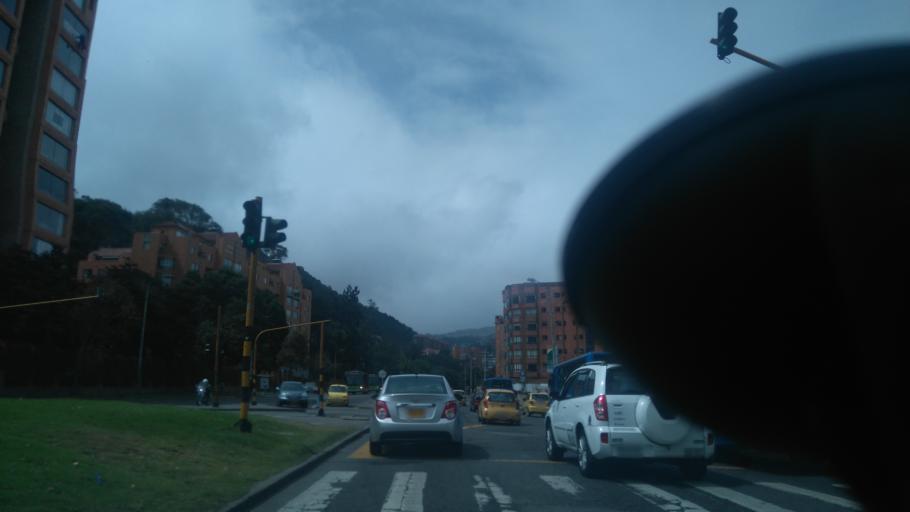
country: CO
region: Bogota D.C.
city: Barrio San Luis
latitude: 4.7121
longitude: -74.0295
